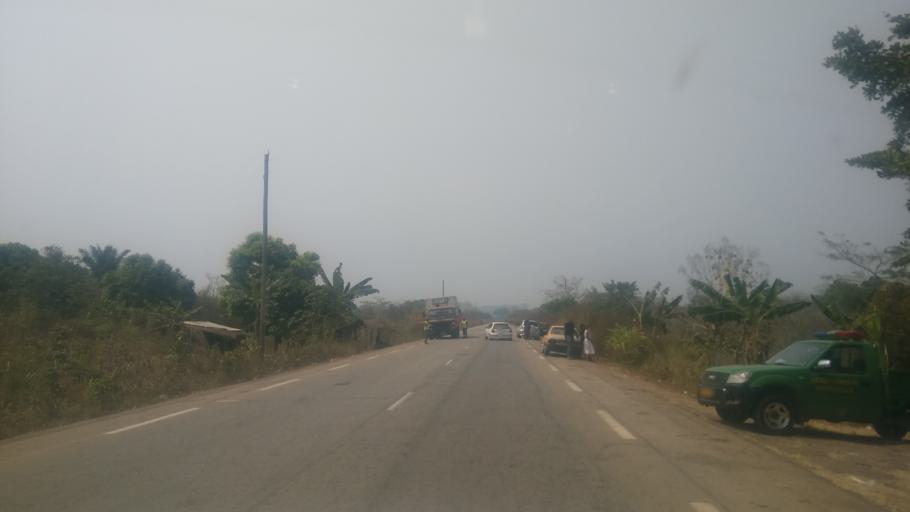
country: CM
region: Centre
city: Bafia
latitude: 4.8281
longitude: 11.0517
